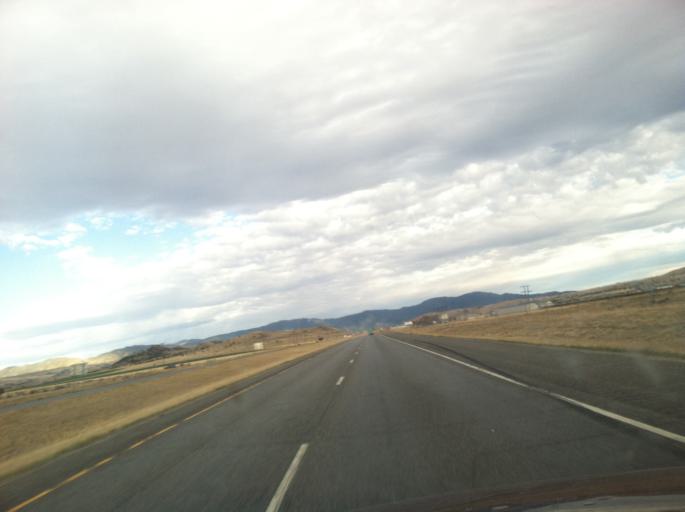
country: US
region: Montana
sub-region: Silver Bow County
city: Butte-Silver Bow (Balance)
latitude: 46.0096
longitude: -112.6826
